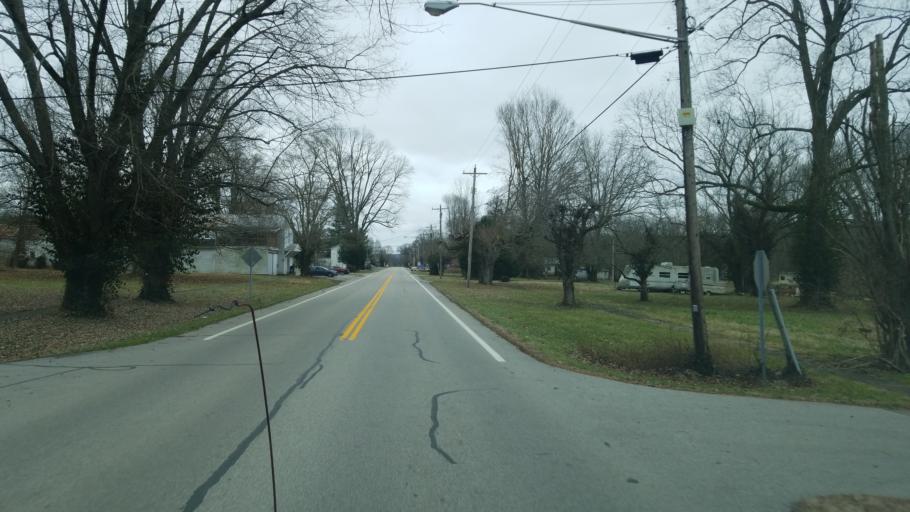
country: US
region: Ohio
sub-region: Clermont County
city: New Richmond
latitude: 38.8109
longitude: -84.2138
